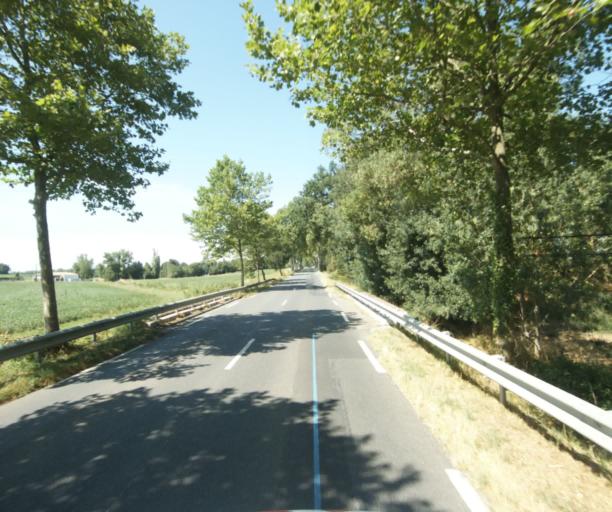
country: FR
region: Midi-Pyrenees
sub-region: Departement de la Haute-Garonne
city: Revel
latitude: 43.4824
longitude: 2.0143
